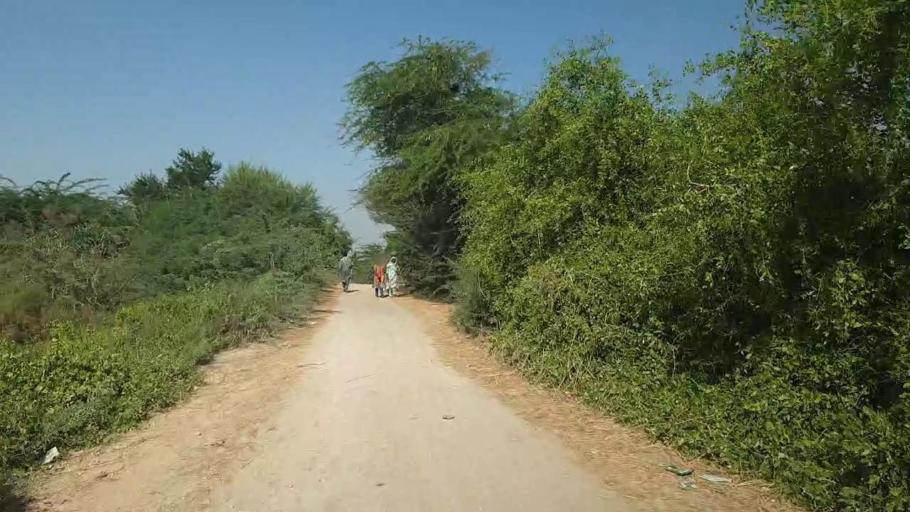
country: PK
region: Sindh
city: Talhar
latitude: 24.7919
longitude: 68.7969
